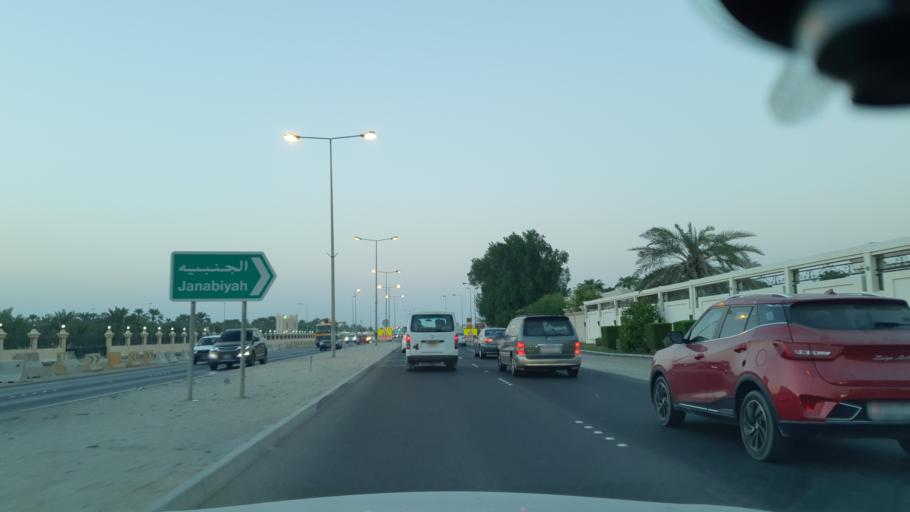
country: BH
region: Central Governorate
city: Madinat Hamad
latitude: 26.1801
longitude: 50.4657
